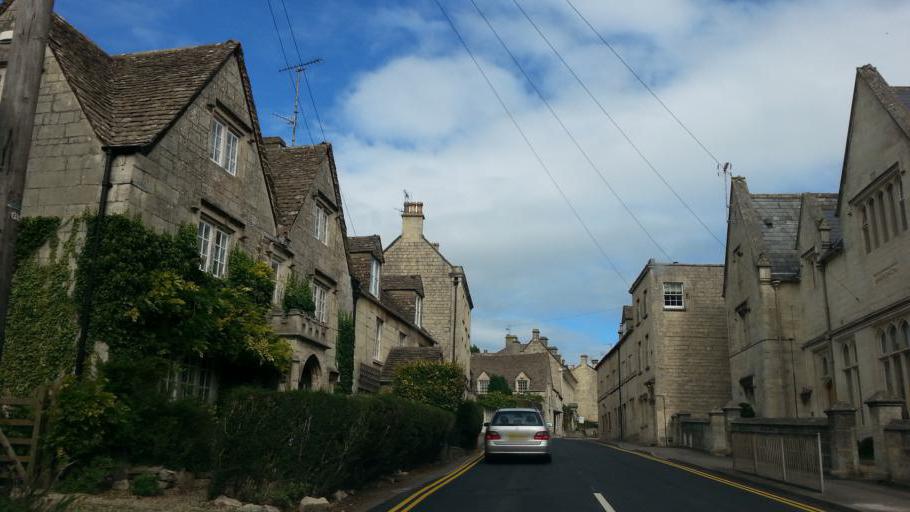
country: GB
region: England
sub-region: Gloucestershire
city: Painswick
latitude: 51.7848
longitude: -2.1965
